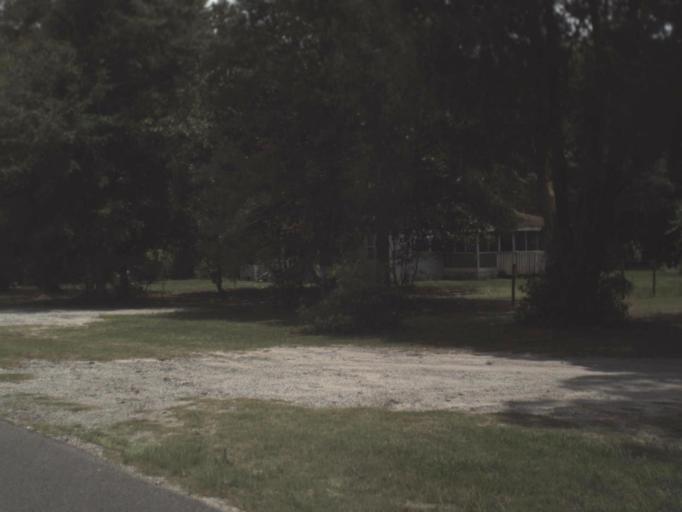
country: US
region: Florida
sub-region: Taylor County
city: Perry
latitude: 30.1033
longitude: -83.6119
